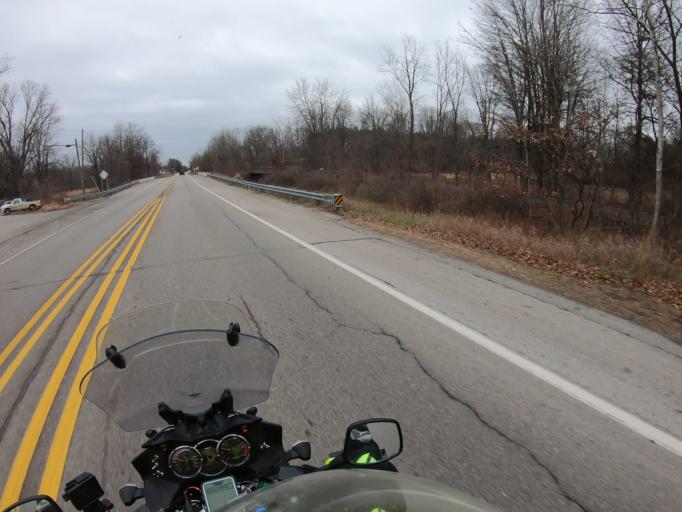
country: US
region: Michigan
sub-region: Saginaw County
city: Saint Charles
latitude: 43.3098
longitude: -84.1421
